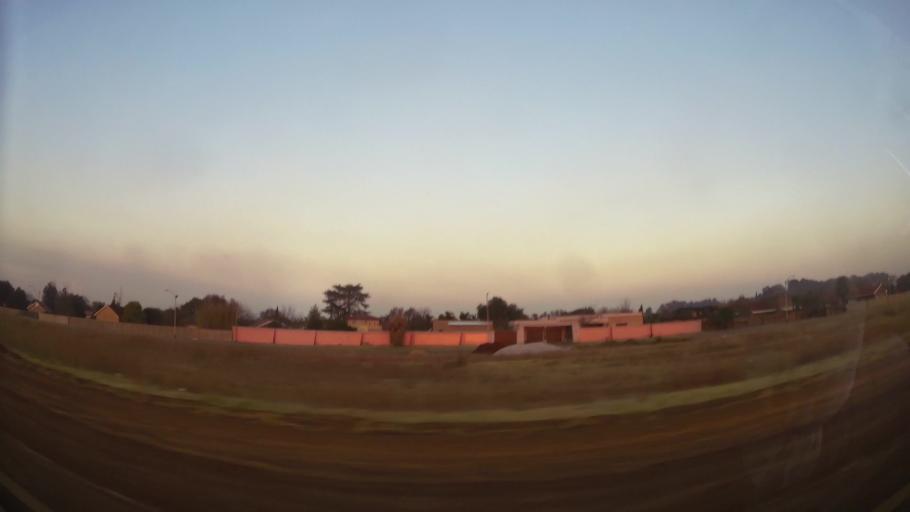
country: ZA
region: Gauteng
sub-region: Ekurhuleni Metropolitan Municipality
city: Springs
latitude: -26.3453
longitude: 28.4161
